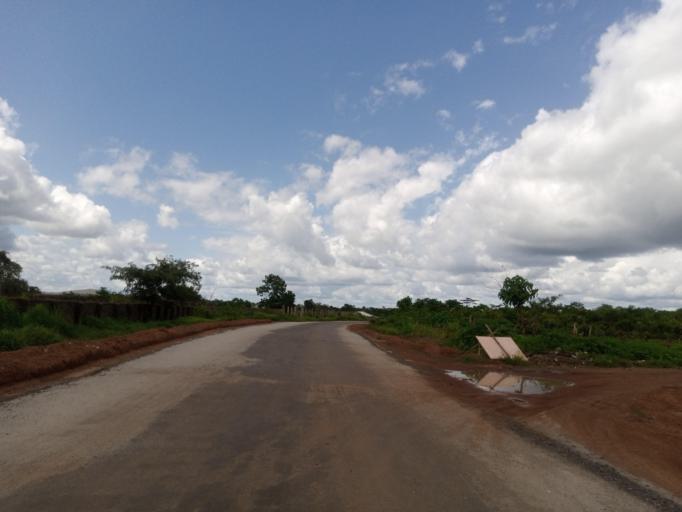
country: SL
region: Northern Province
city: Port Loko
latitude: 8.7757
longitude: -12.7705
